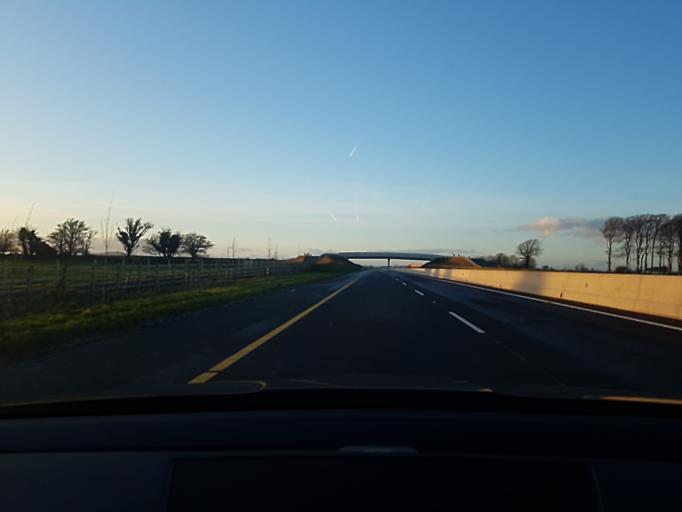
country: IE
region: Connaught
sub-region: County Galway
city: Tuam
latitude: 53.4633
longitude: -8.8539
